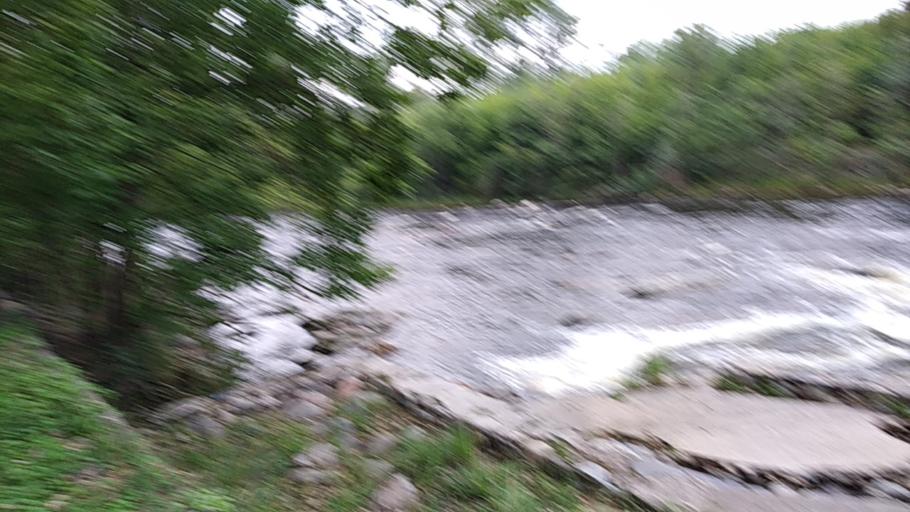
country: AR
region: Cordoba
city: Alta Gracia
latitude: -31.7254
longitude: -64.4363
